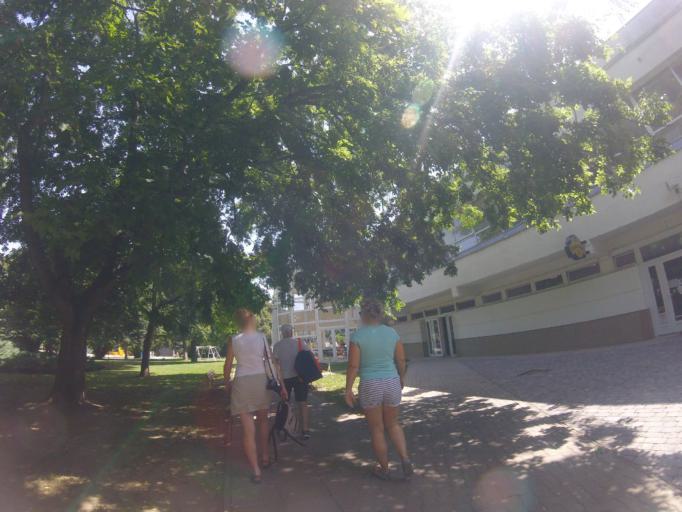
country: HU
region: Baranya
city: Harkany
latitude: 45.8512
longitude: 18.2372
